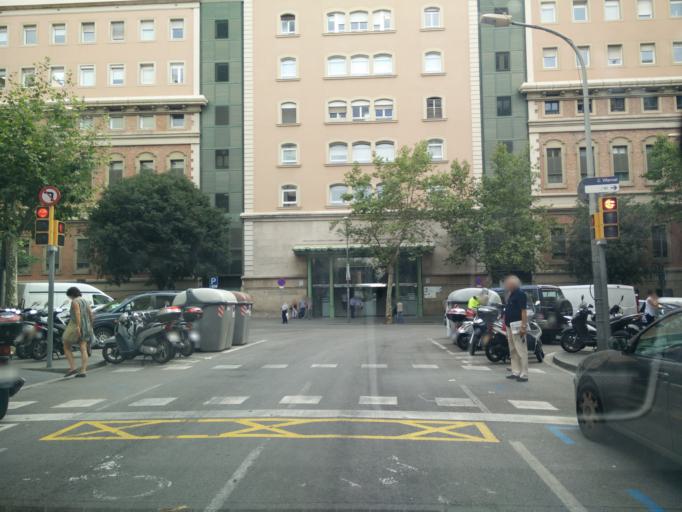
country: ES
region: Catalonia
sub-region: Provincia de Barcelona
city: Barcelona
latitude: 41.3888
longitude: 2.1515
